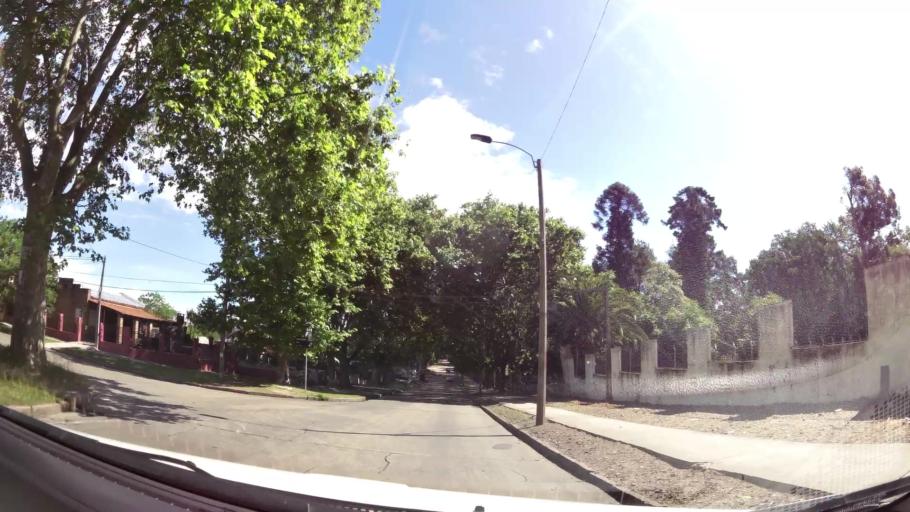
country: UY
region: Montevideo
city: Montevideo
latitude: -34.8416
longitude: -56.1979
